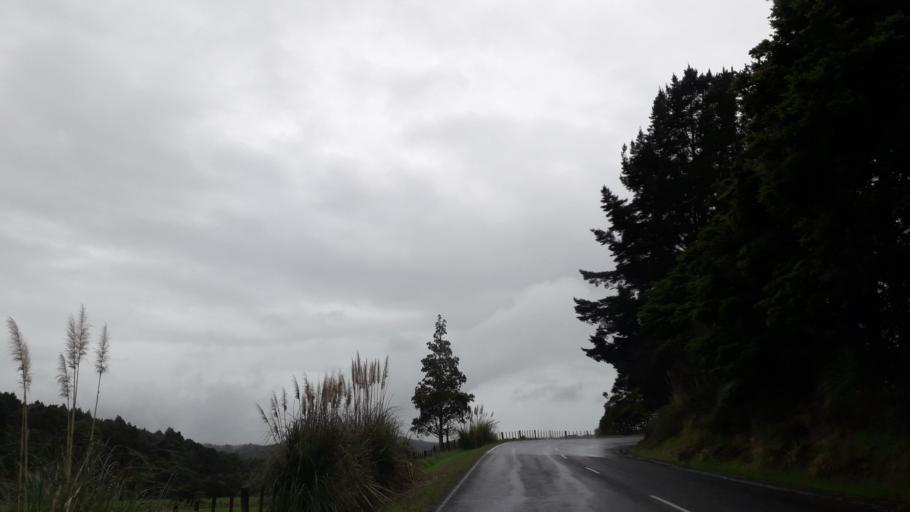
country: NZ
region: Northland
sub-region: Far North District
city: Kaitaia
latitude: -35.3590
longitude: 173.4839
